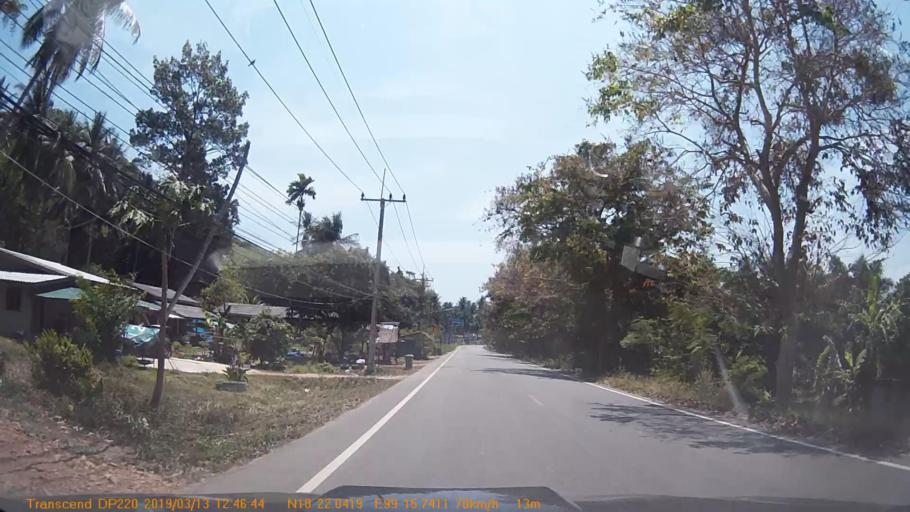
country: TH
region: Chumphon
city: Chumphon
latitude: 10.3670
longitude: 99.2623
